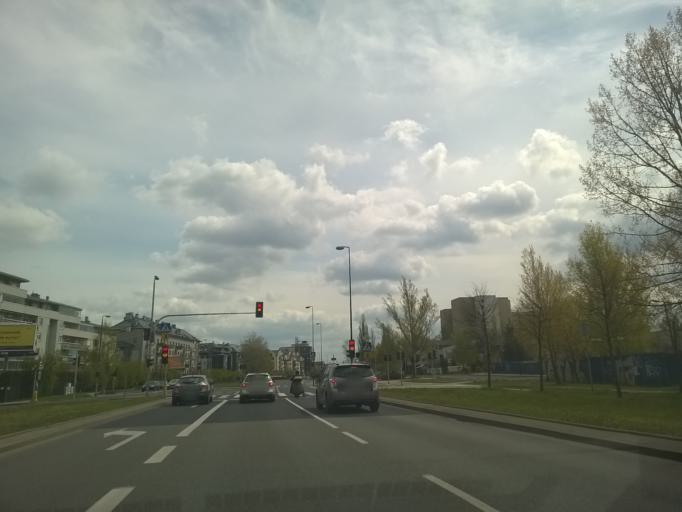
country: PL
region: Masovian Voivodeship
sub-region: Warszawa
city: Ursynow
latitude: 52.1529
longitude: 21.0556
